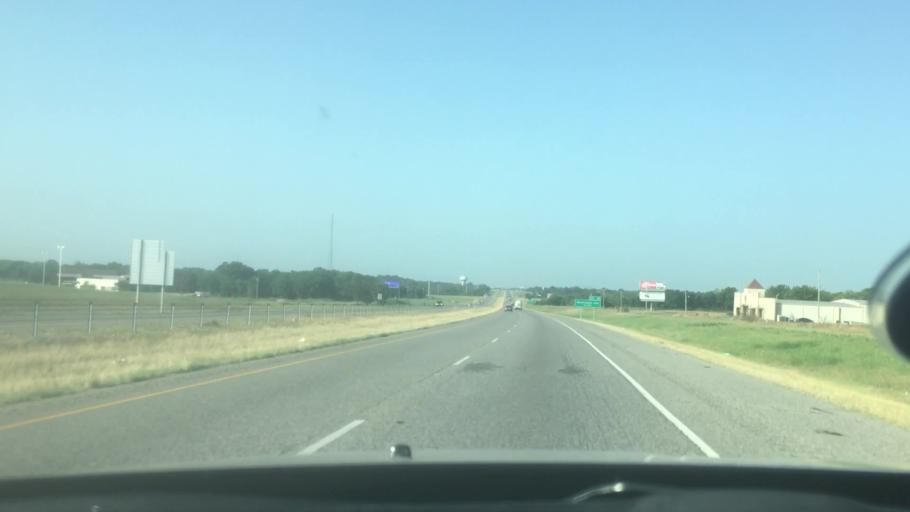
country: US
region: Oklahoma
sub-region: Bryan County
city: Durant
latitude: 34.0307
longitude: -96.3829
